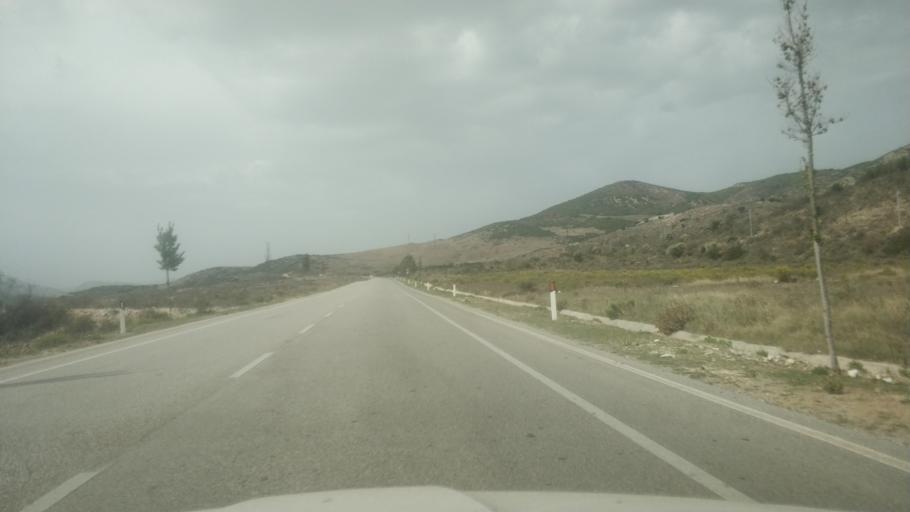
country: AL
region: Gjirokaster
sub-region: Rrethi i Tepelenes
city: Memaliaj
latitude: 40.3590
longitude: 19.9314
